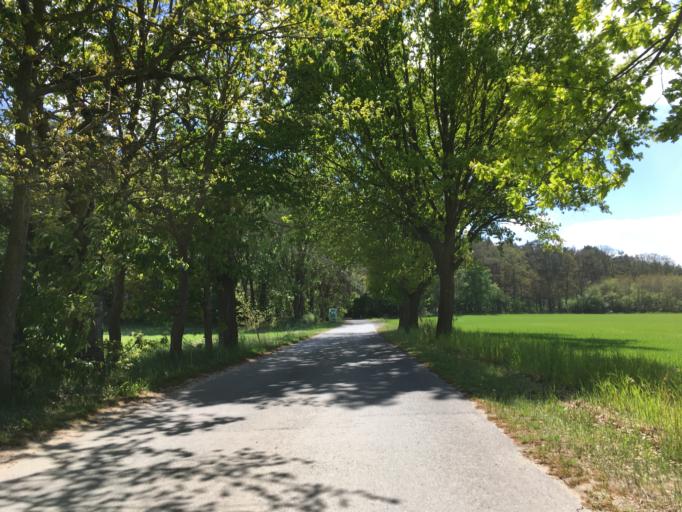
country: DE
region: Brandenburg
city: Rudnitz
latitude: 52.7252
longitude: 13.6593
